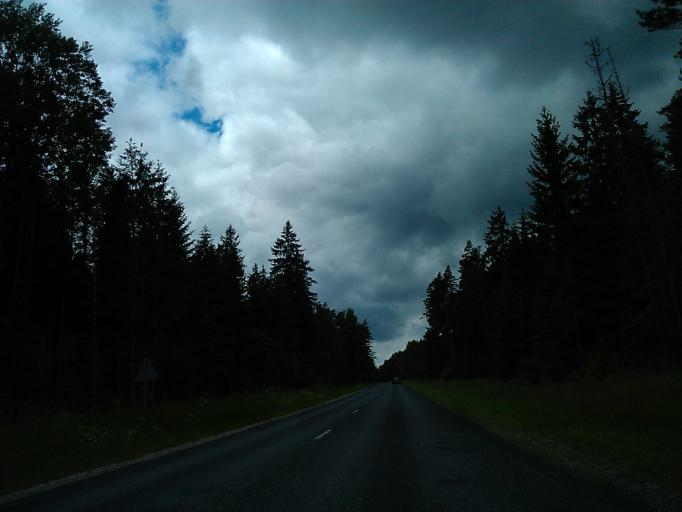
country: LV
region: Talsu Rajons
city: Stende
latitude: 57.0905
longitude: 22.3955
